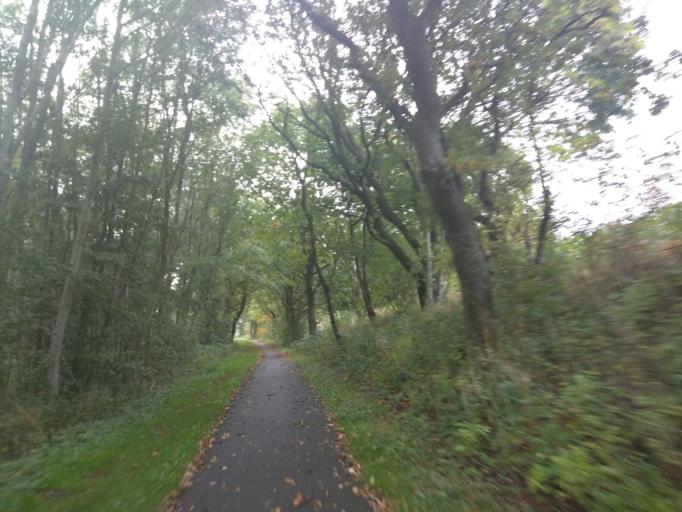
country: DK
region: Central Jutland
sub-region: Silkeborg Kommune
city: Silkeborg
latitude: 56.2314
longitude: 9.5193
